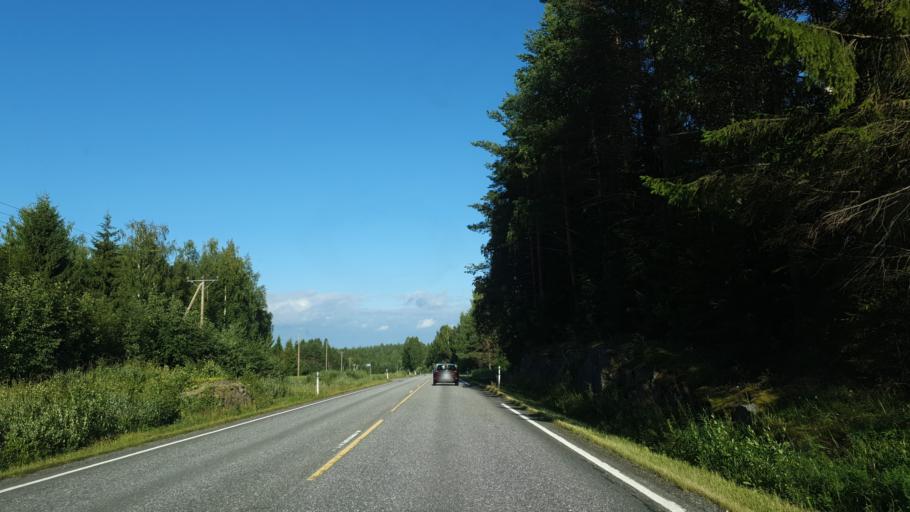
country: FI
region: North Karelia
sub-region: Joensuu
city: Outokumpu
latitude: 62.5337
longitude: 28.9263
